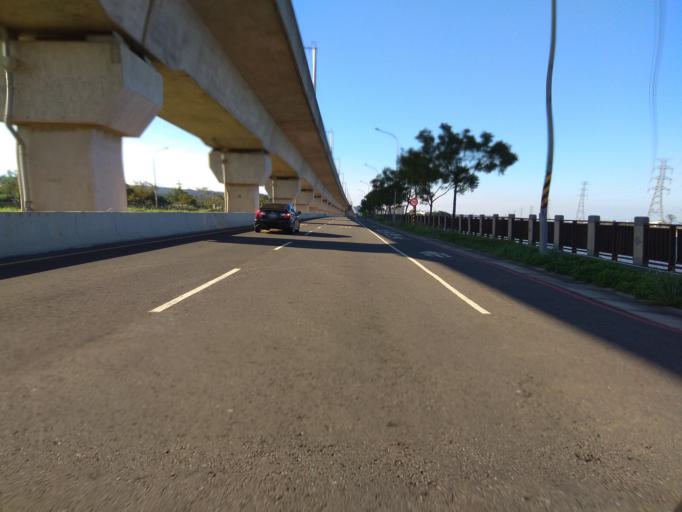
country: TW
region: Taiwan
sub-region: Hsinchu
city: Zhubei
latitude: 24.9054
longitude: 121.0849
